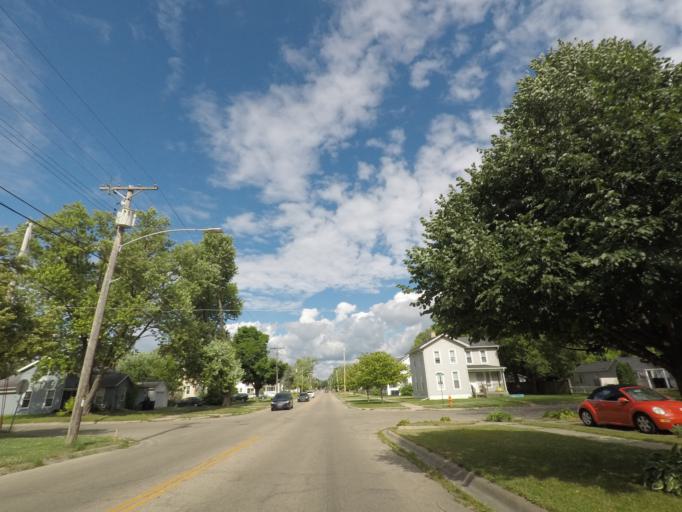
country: US
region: Wisconsin
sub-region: Rock County
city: Janesville
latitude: 42.6742
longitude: -89.0283
